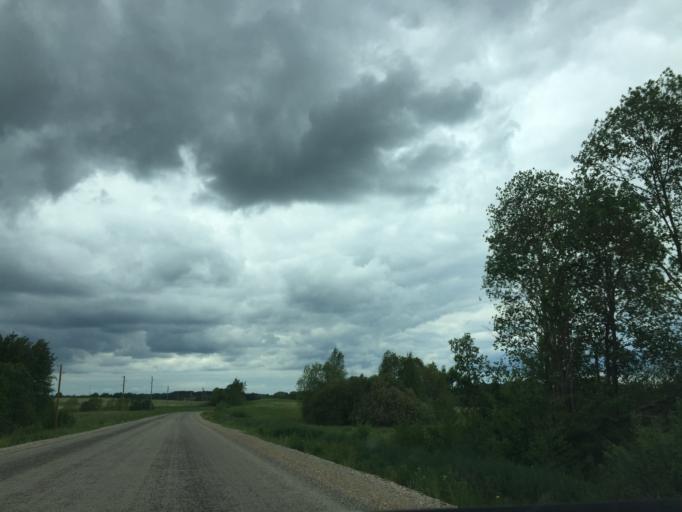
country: LV
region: Dagda
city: Dagda
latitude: 56.0717
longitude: 27.5517
